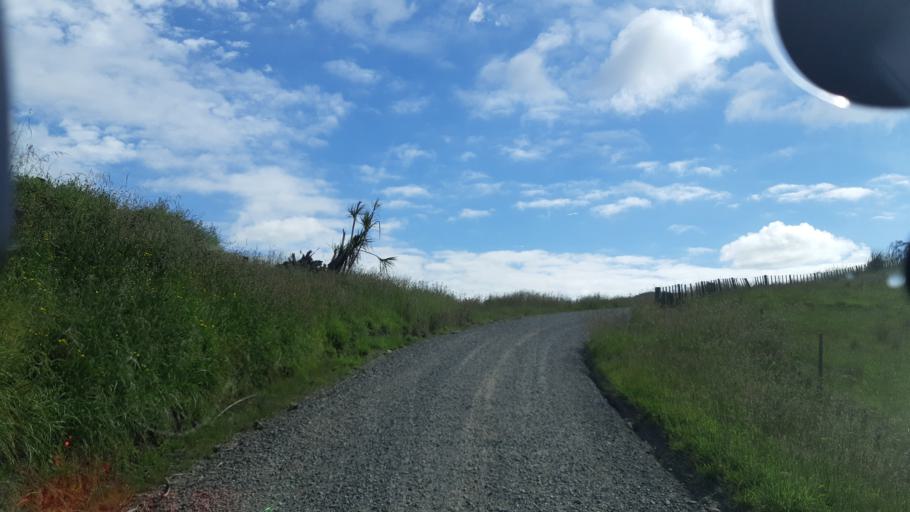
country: NZ
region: Manawatu-Wanganui
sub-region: Rangitikei District
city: Bulls
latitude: -39.9614
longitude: 175.4762
